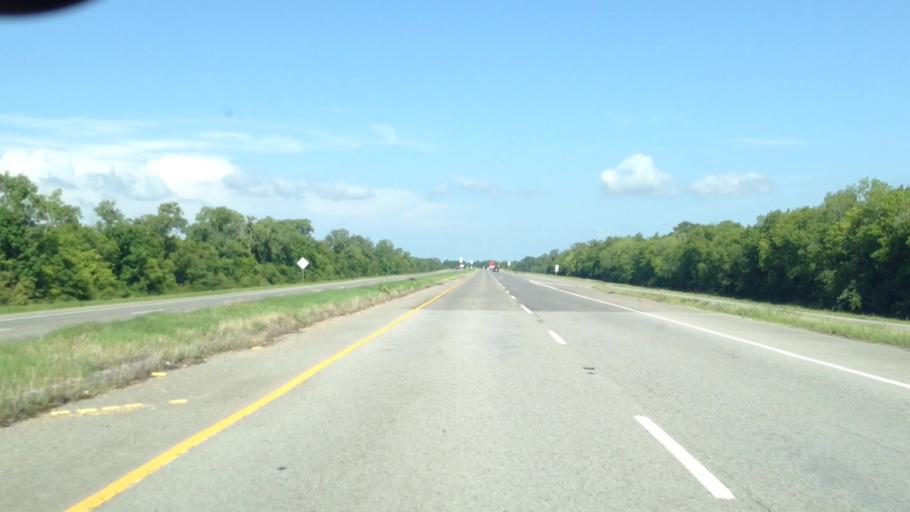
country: US
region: Louisiana
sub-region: Saint Landry Parish
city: Krotz Springs
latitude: 30.5460
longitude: -91.8147
